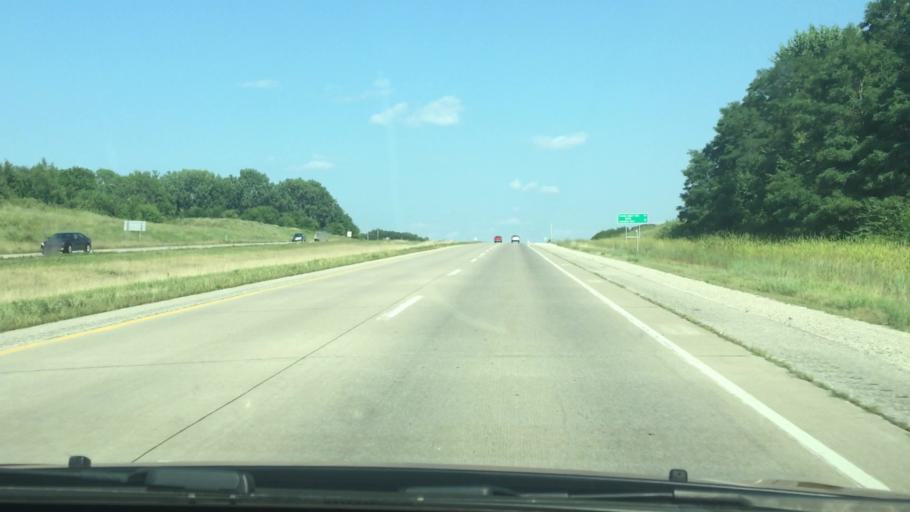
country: US
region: Iowa
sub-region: Scott County
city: Blue Grass
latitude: 41.5127
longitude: -90.7993
